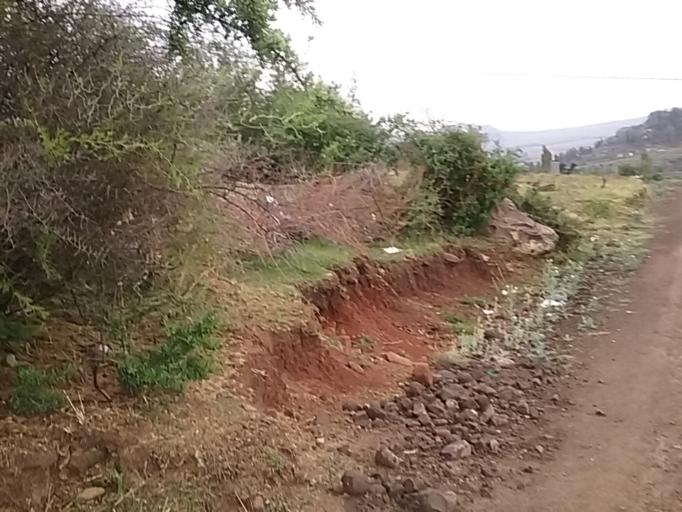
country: LS
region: Berea
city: Teyateyaneng
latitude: -29.1356
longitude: 27.7392
